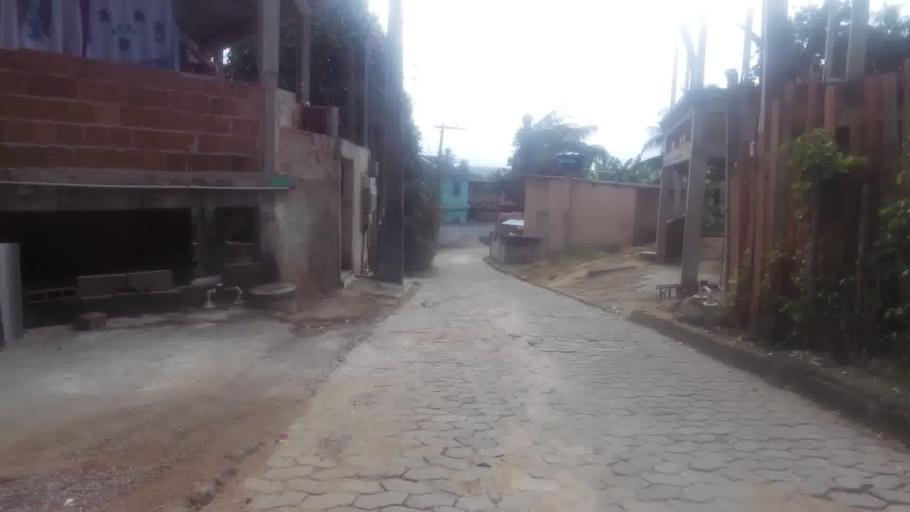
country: BR
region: Espirito Santo
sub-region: Guarapari
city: Guarapari
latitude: -20.7627
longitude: -40.5759
